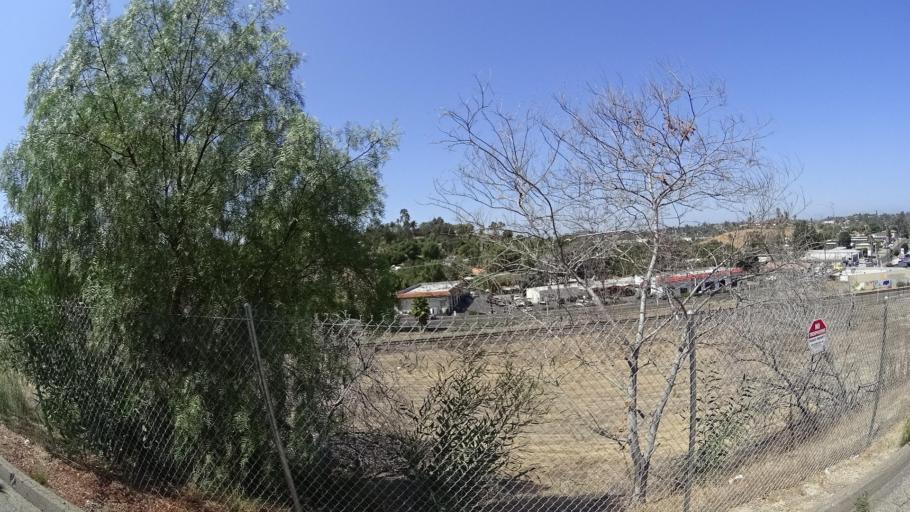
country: US
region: California
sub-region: San Diego County
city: Lake San Marcos
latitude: 33.1671
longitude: -117.2046
